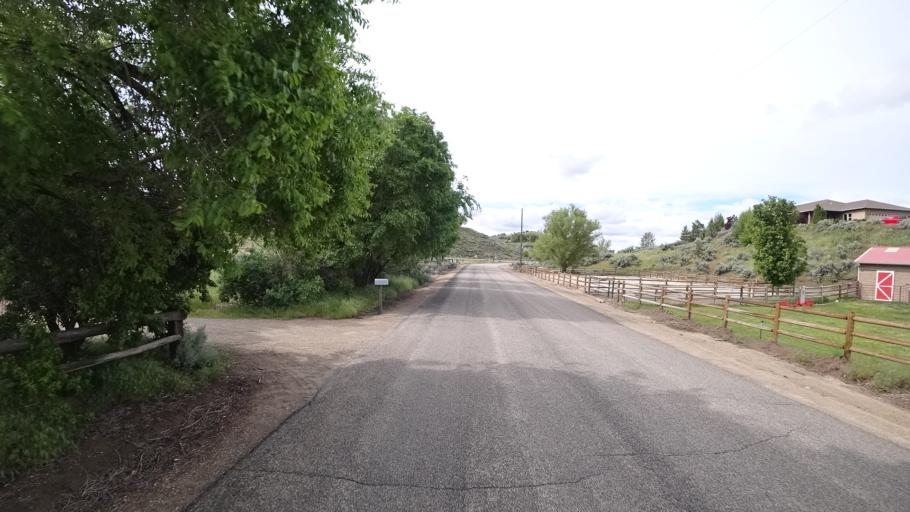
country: US
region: Idaho
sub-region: Ada County
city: Eagle
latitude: 43.7465
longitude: -116.3571
